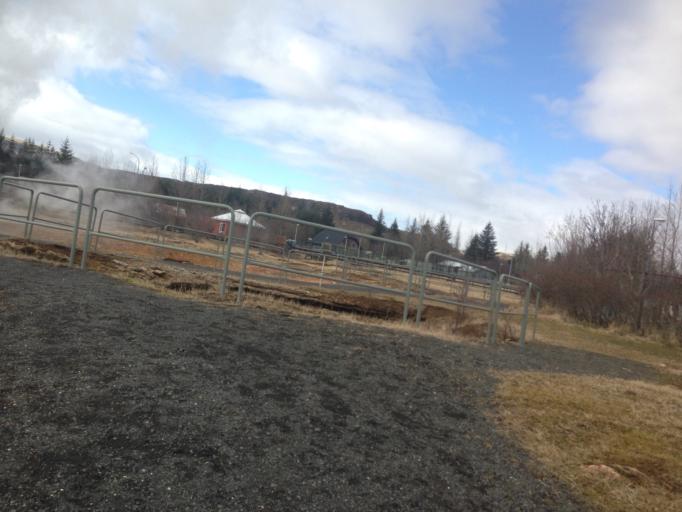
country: IS
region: South
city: Hveragerdi
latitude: 64.0013
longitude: -21.1880
